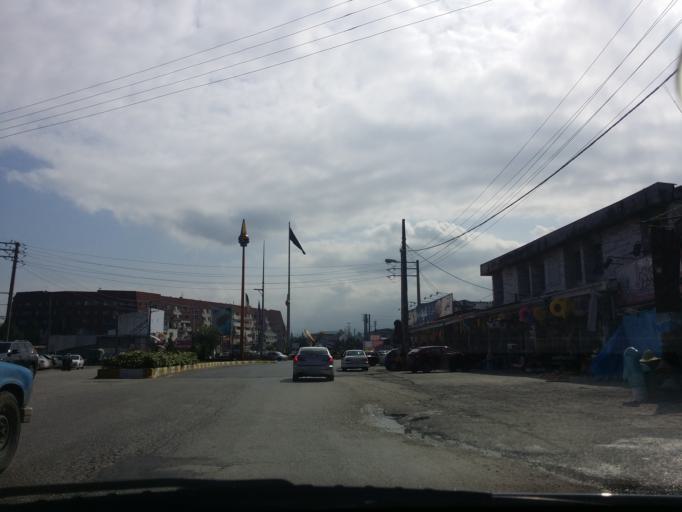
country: IR
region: Mazandaran
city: Chalus
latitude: 36.6831
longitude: 51.4012
